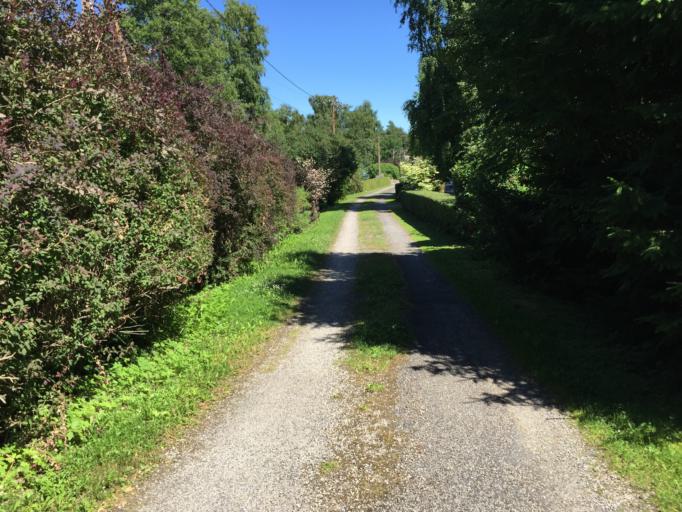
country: EE
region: Harju
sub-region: Kuusalu vald
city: Kuusalu
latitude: 59.4978
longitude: 25.3041
